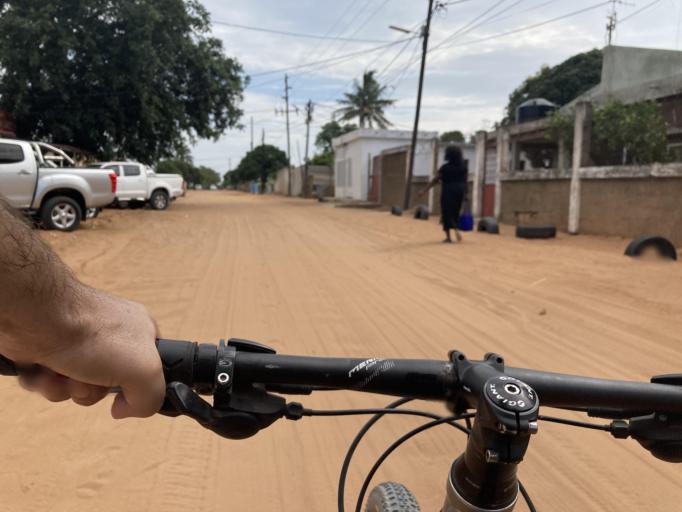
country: MZ
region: Maputo City
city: Maputo
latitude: -25.8960
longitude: 32.6071
